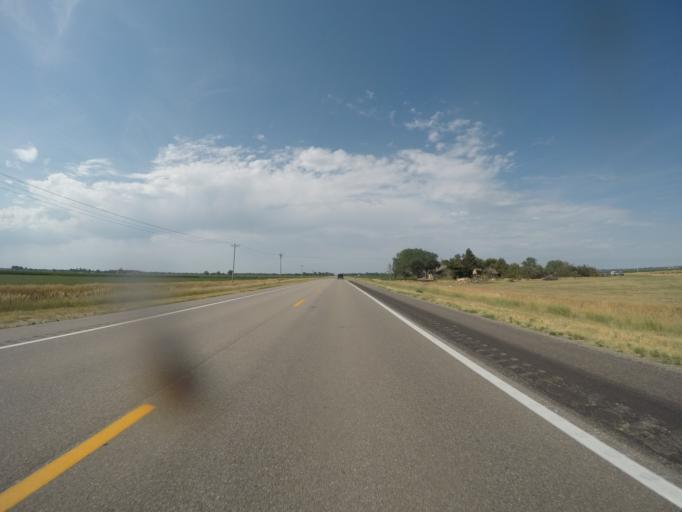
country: US
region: Nebraska
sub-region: Kearney County
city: Minden
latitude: 40.6326
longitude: -98.9514
